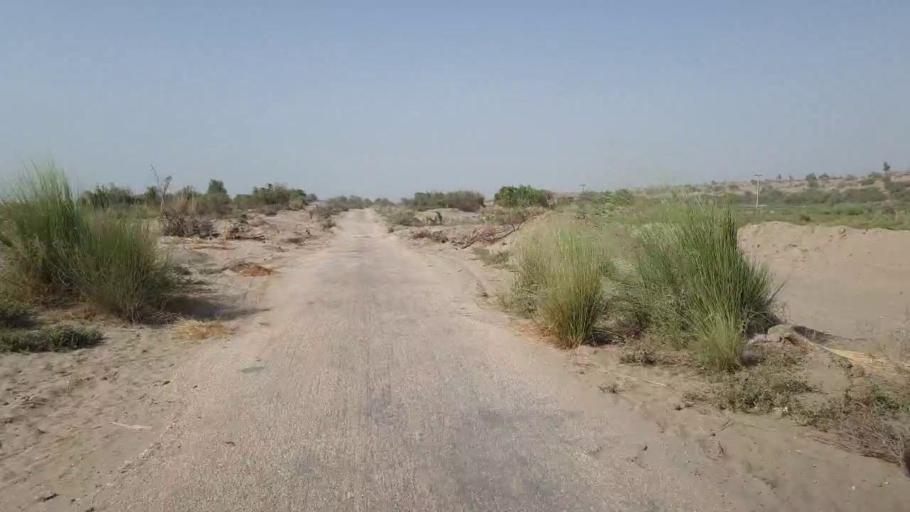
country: PK
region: Sindh
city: Jam Sahib
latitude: 26.6018
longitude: 68.9261
